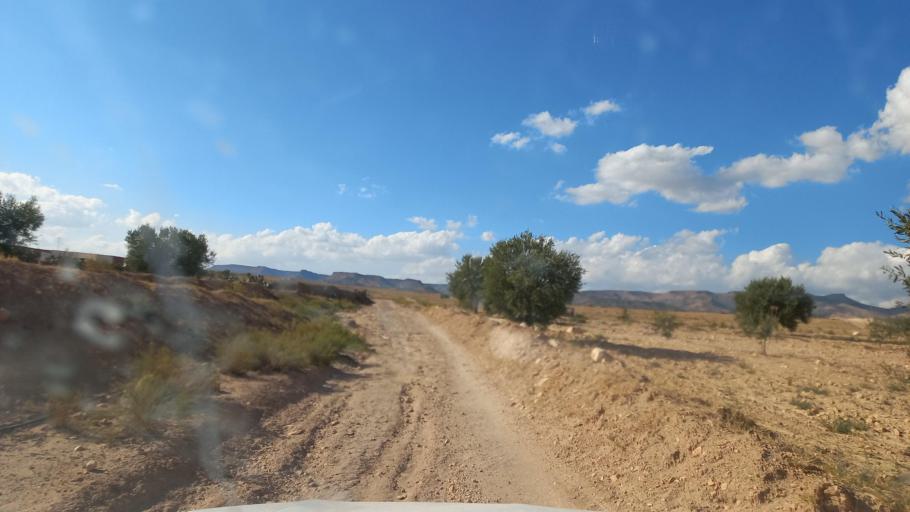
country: TN
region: Al Qasrayn
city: Sbiba
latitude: 35.3964
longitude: 9.0336
